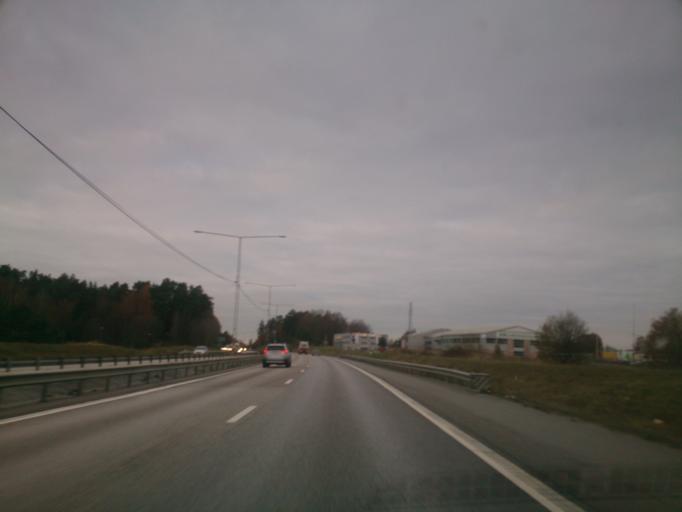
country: SE
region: Stockholm
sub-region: Upplands Vasby Kommun
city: Upplands Vaesby
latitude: 59.5217
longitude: 17.9267
